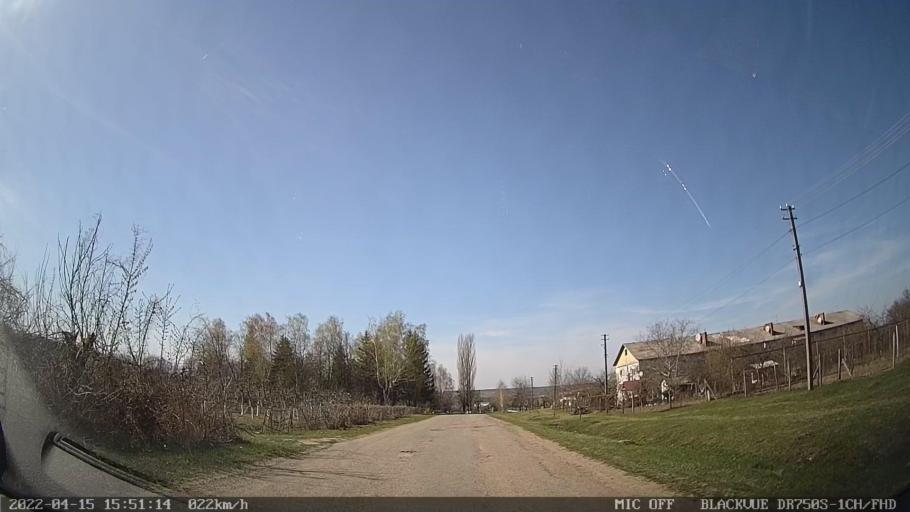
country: MD
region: Raionul Ocnita
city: Otaci
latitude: 48.3936
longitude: 27.8990
